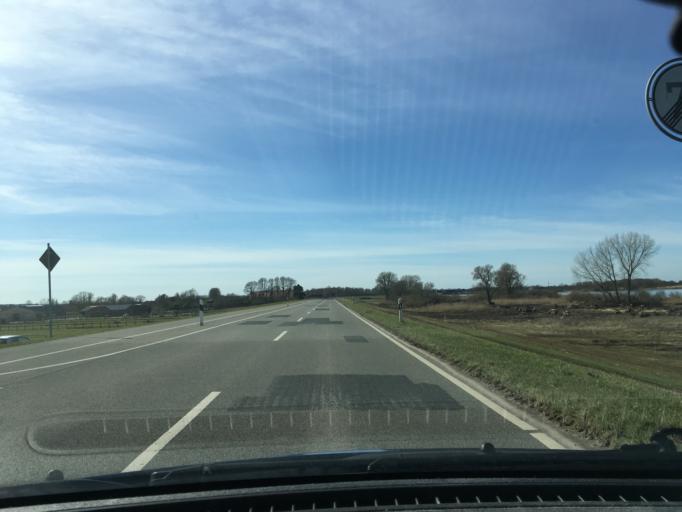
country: DE
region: Lower Saxony
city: Winsen
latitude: 53.3938
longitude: 10.2142
